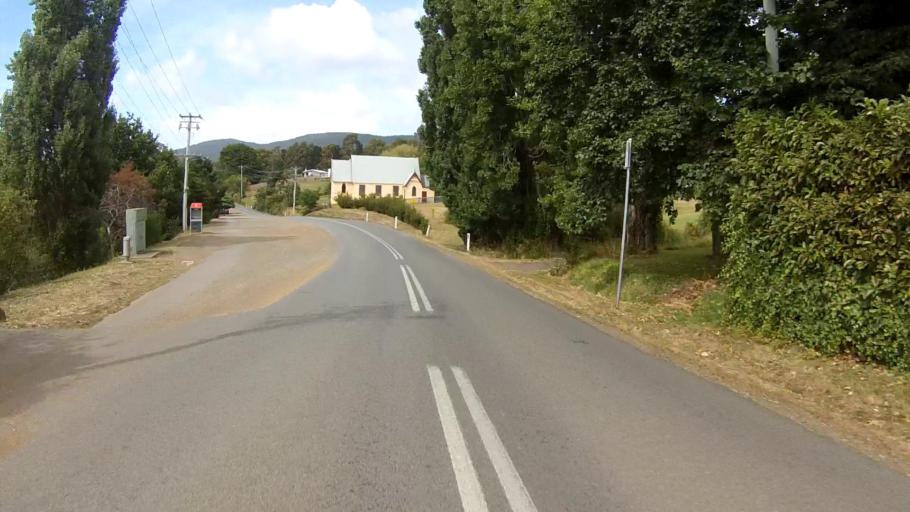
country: AU
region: Tasmania
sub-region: Kingborough
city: Kettering
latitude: -43.1605
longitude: 147.2384
